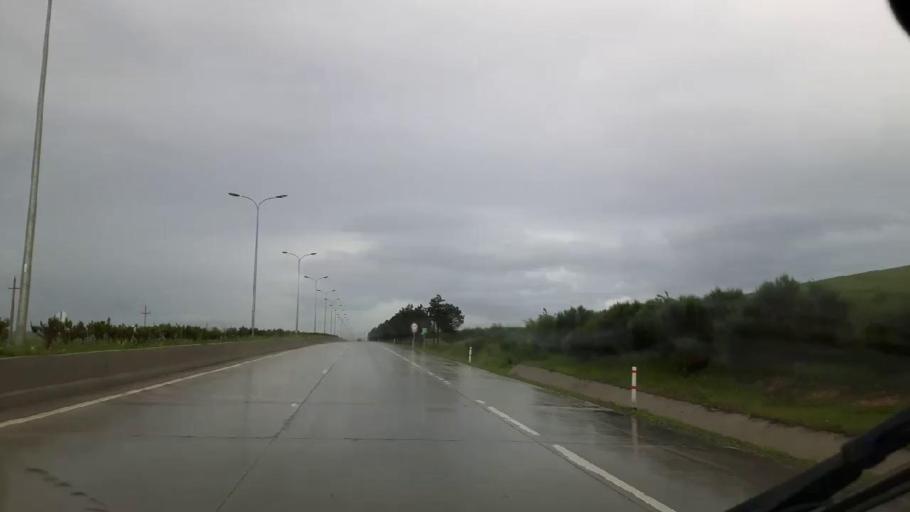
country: GE
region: Shida Kartli
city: Gori
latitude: 42.0181
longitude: 44.0194
